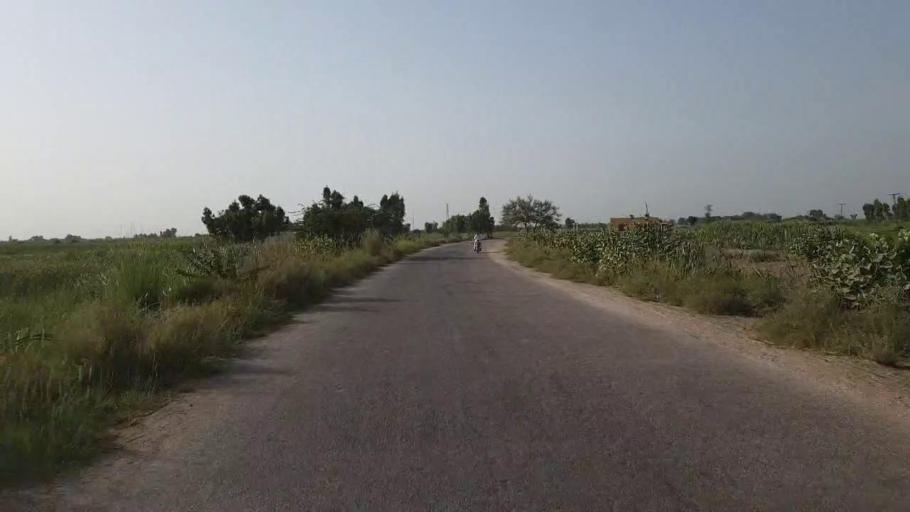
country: PK
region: Sindh
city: Jam Sahib
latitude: 26.4187
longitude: 68.8705
